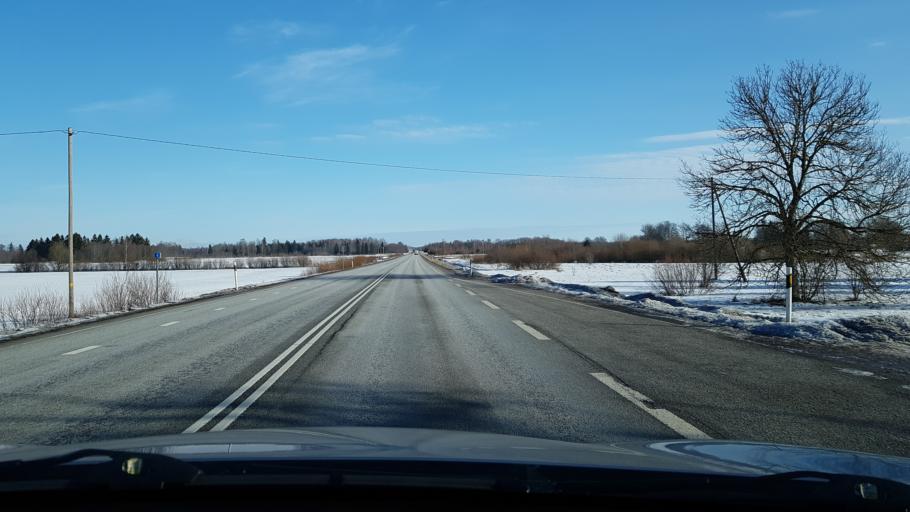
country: EE
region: Viljandimaa
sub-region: Vohma linn
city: Vohma
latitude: 58.6832
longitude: 25.6850
